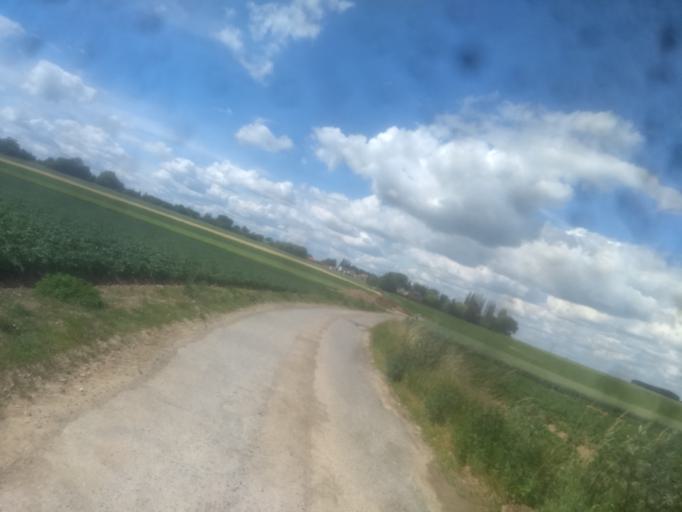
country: FR
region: Nord-Pas-de-Calais
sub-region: Departement du Pas-de-Calais
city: Tilloy-les-Mofflaines
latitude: 50.2432
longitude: 2.8293
